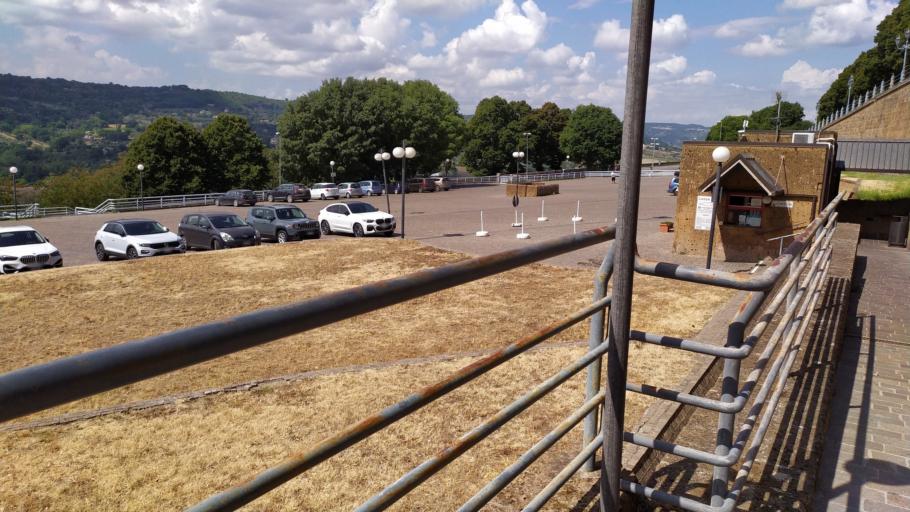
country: IT
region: Umbria
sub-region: Provincia di Terni
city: Orvieto
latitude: 42.7169
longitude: 12.1056
